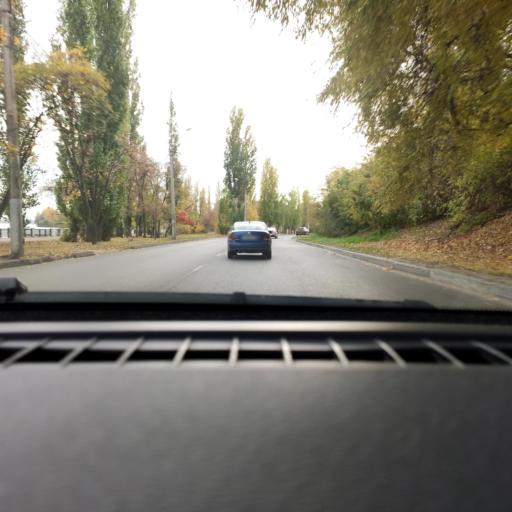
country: RU
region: Voronezj
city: Voronezh
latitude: 51.6628
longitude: 39.2192
